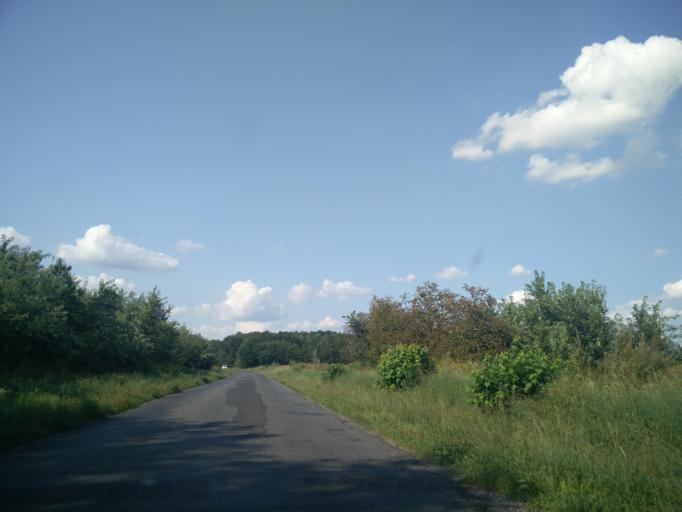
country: HU
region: Zala
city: Zalaegerszeg
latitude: 46.8694
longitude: 16.8032
